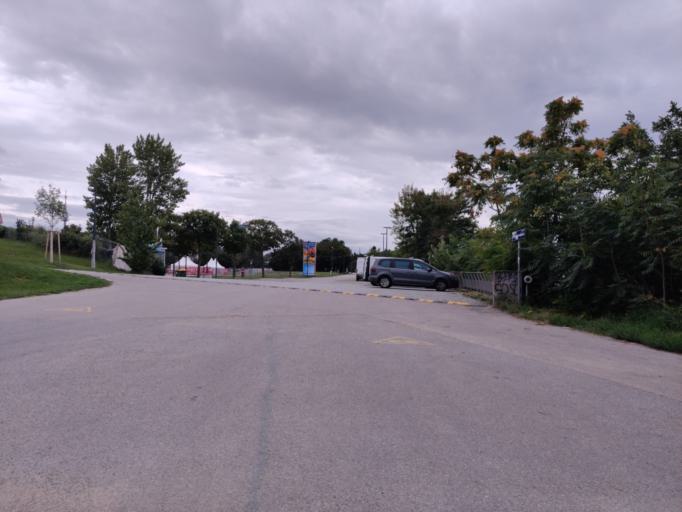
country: AT
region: Vienna
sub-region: Wien Stadt
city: Vienna
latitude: 48.2472
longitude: 16.3869
